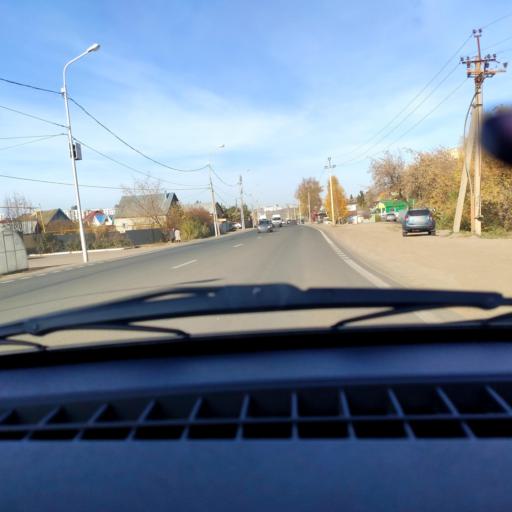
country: RU
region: Bashkortostan
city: Ufa
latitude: 54.6913
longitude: 55.9819
